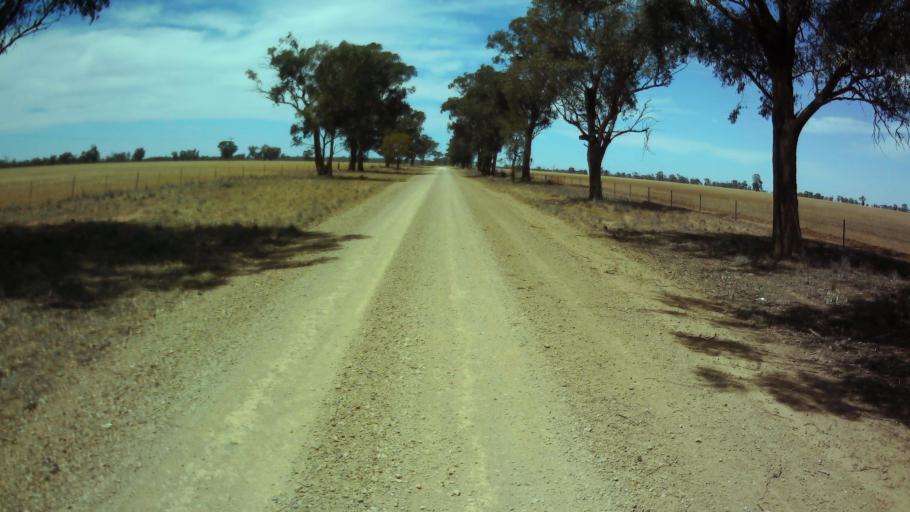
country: AU
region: New South Wales
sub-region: Weddin
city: Grenfell
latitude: -33.8718
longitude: 147.8062
